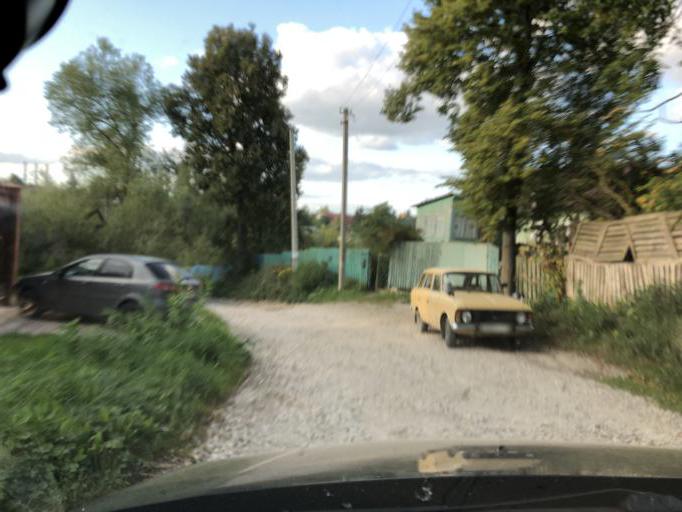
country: RU
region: Tula
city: Kosaya Gora
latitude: 54.1785
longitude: 37.5373
